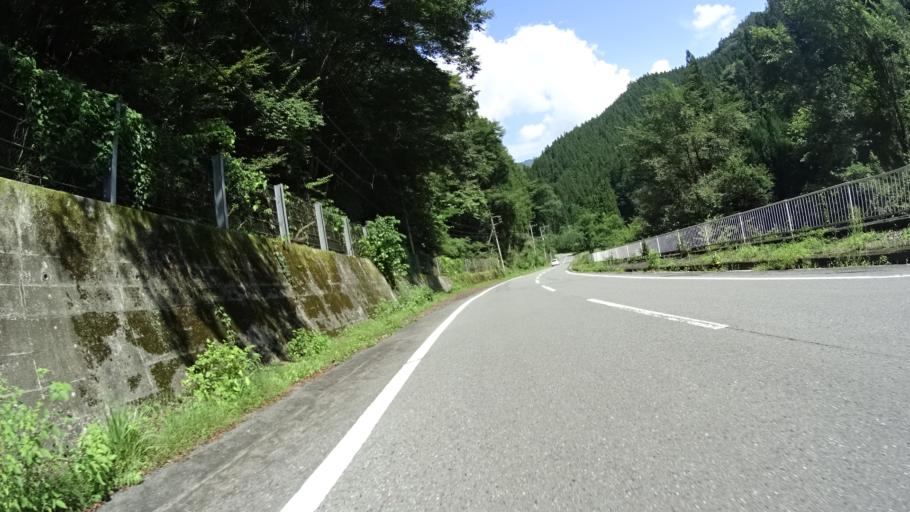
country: JP
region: Gunma
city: Tomioka
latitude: 36.0778
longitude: 138.8250
